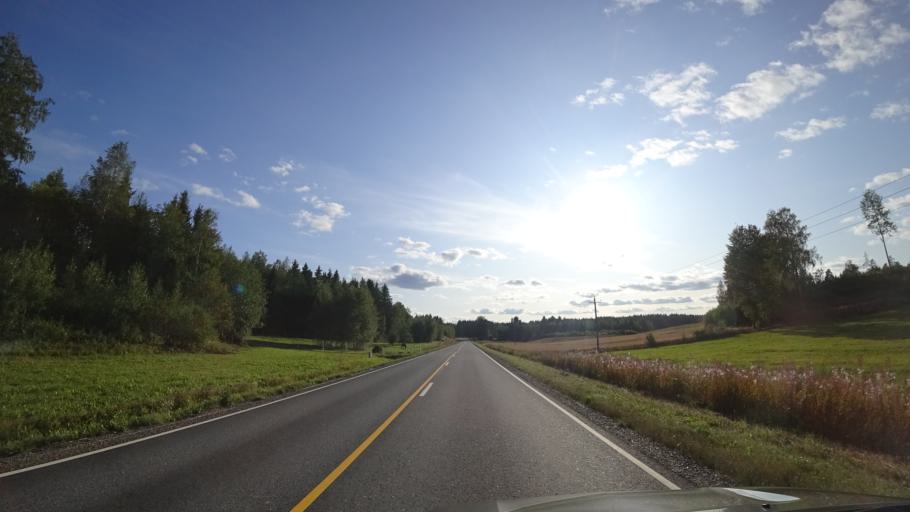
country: FI
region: Paijanne Tavastia
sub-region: Lahti
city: Hollola
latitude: 61.1362
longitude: 25.3068
